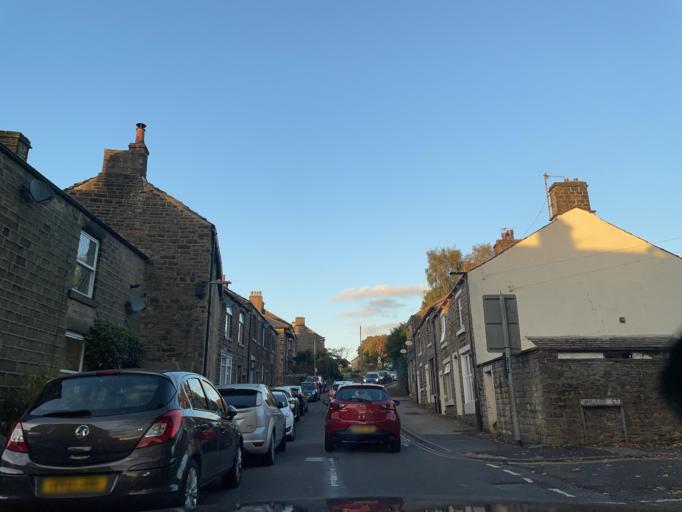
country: GB
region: England
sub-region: Derbyshire
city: Glossop
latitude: 53.4609
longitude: -1.9711
